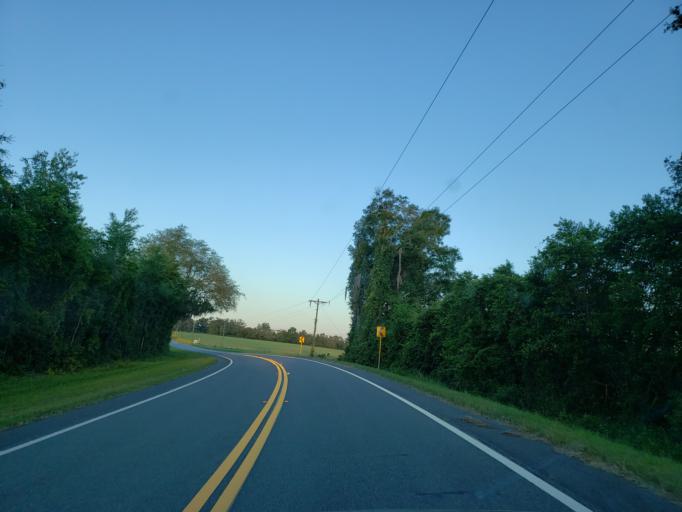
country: US
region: Florida
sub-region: Madison County
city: Madison
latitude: 30.5815
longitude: -83.2393
